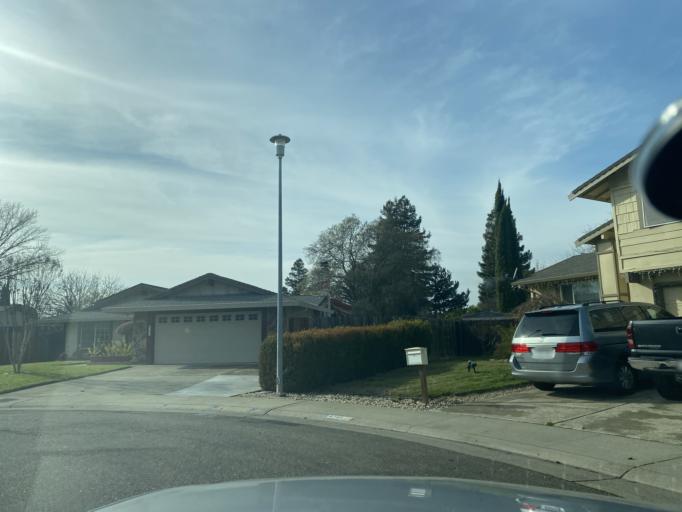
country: US
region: California
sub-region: Sacramento County
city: Elk Grove
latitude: 38.3998
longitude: -121.3789
